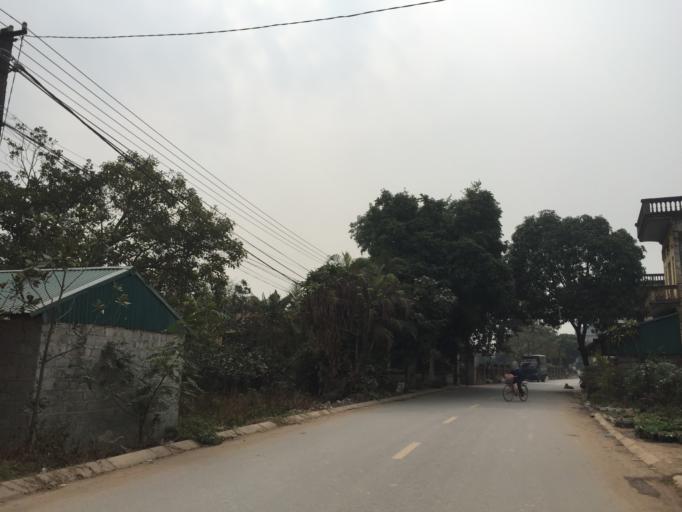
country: VN
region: Hung Yen
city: Van Giang
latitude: 20.9585
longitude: 105.9103
